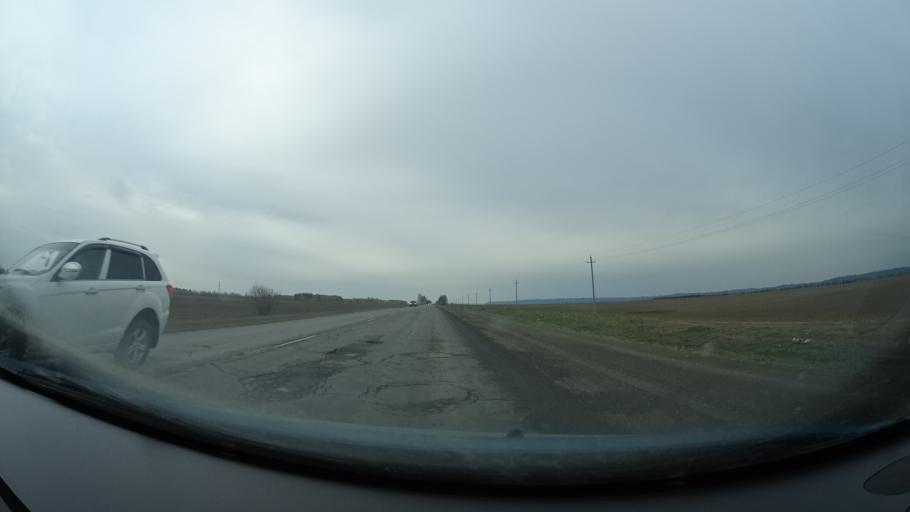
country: RU
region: Perm
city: Ust'-Kachka
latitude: 58.0655
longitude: 55.6221
